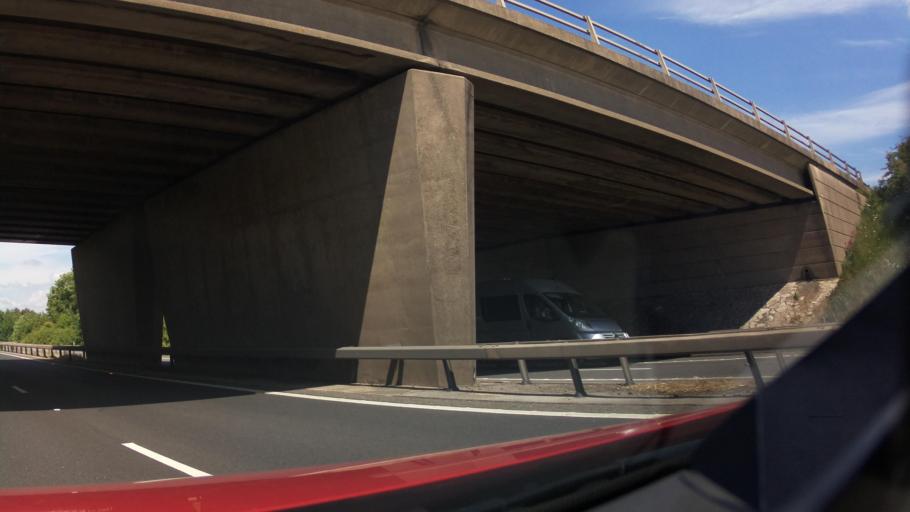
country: GB
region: England
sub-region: North Lincolnshire
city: Gunness
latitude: 53.5563
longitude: -0.7102
